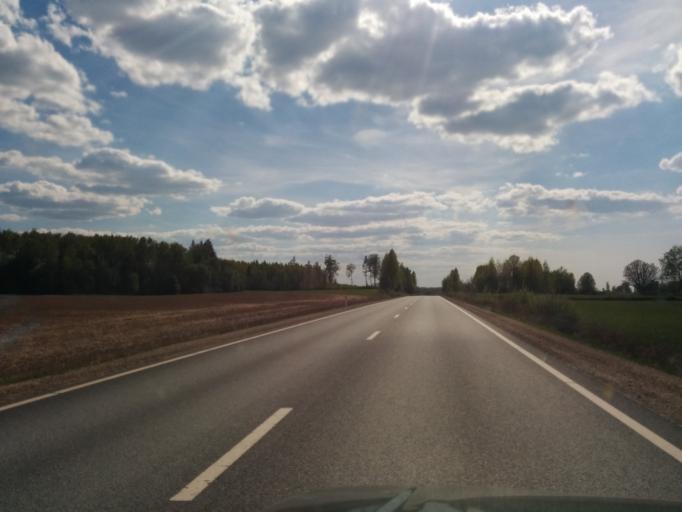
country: LV
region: Sigulda
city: Sigulda
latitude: 57.2465
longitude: 24.8444
